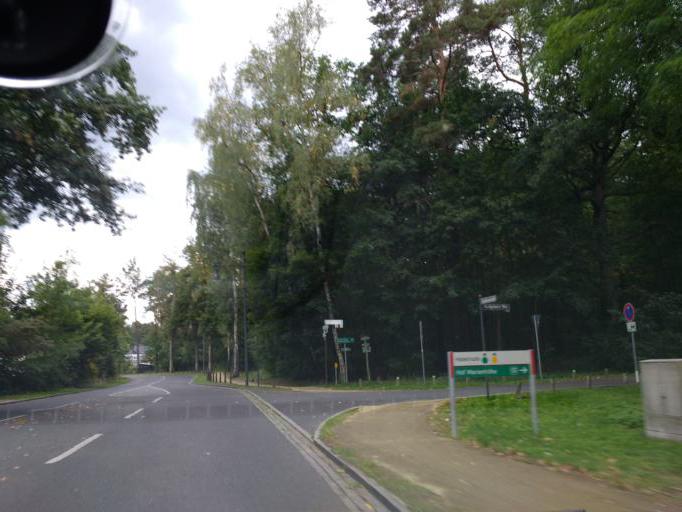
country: DE
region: Brandenburg
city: Bad Saarow
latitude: 52.2926
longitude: 14.0449
